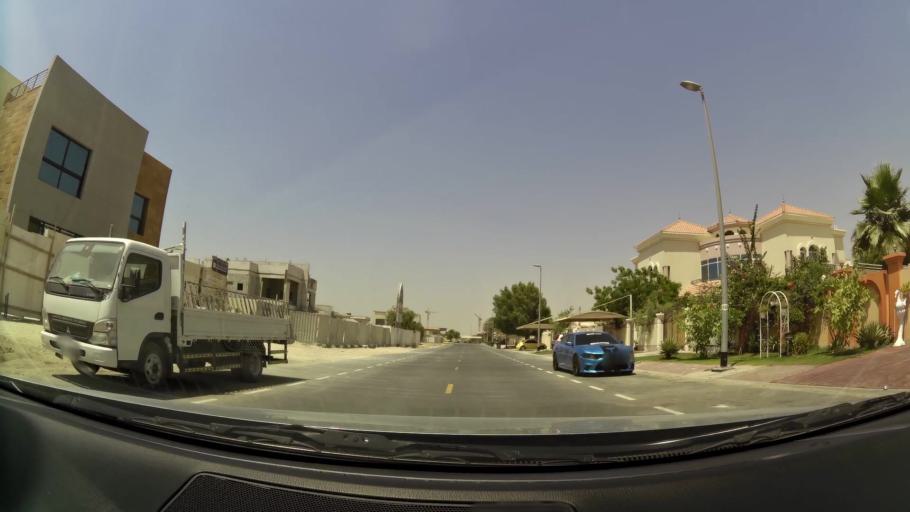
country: AE
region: Dubai
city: Dubai
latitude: 25.0991
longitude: 55.2234
